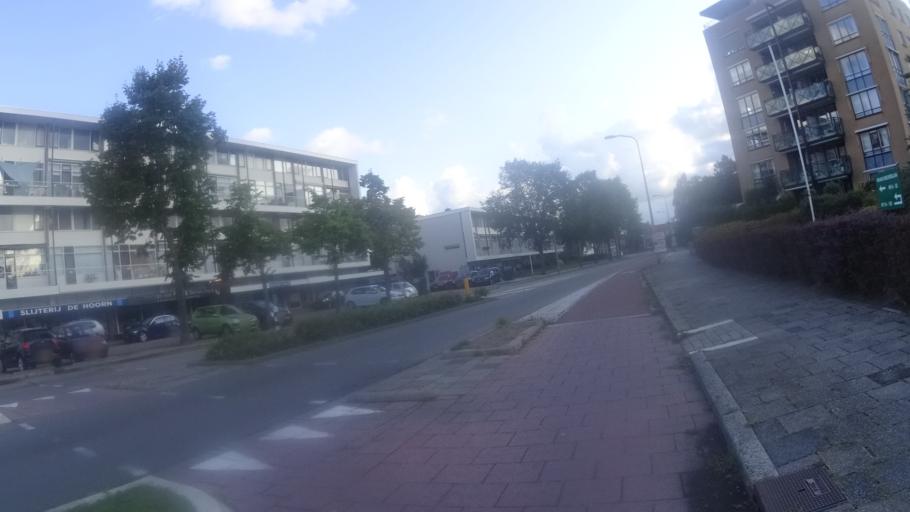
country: NL
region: South Holland
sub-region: Gemeente Katwijk
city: Katwijk aan Zee
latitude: 52.1992
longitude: 4.4064
